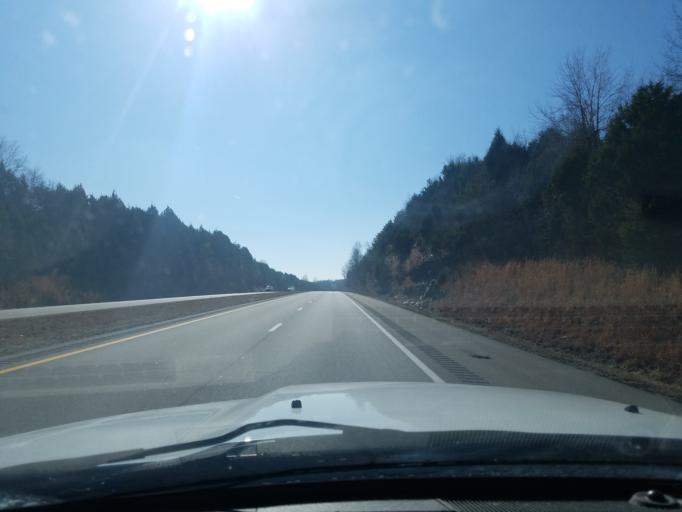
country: US
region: Kentucky
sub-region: Grayson County
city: Leitchfield
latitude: 37.5206
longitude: -86.1481
